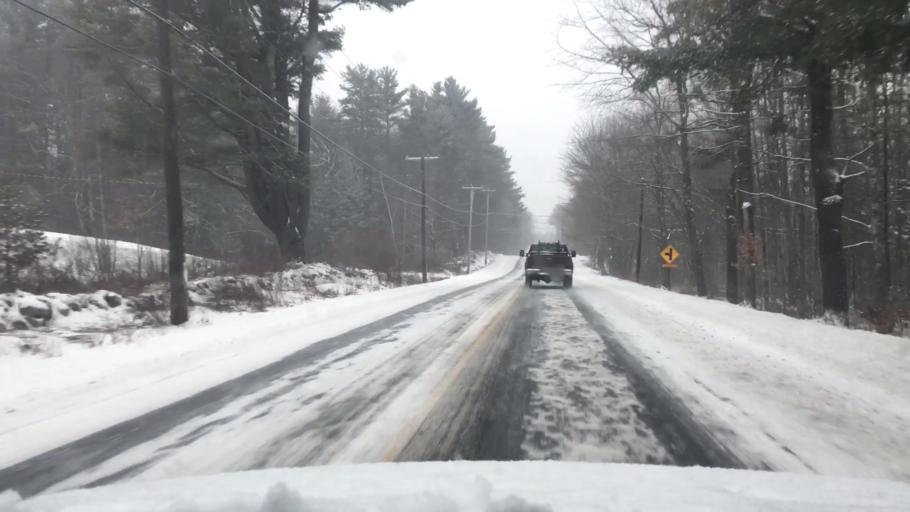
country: US
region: Maine
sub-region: Cumberland County
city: Cumberland Center
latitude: 43.8359
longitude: -70.3208
